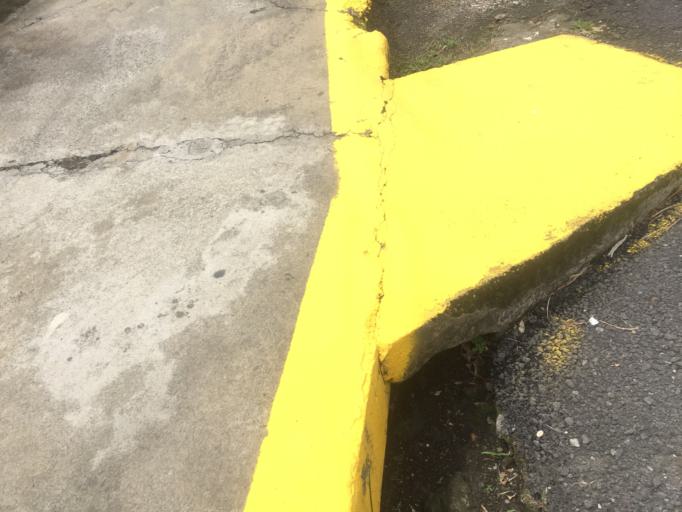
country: CR
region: Heredia
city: Heredia
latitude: 10.0043
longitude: -84.1201
